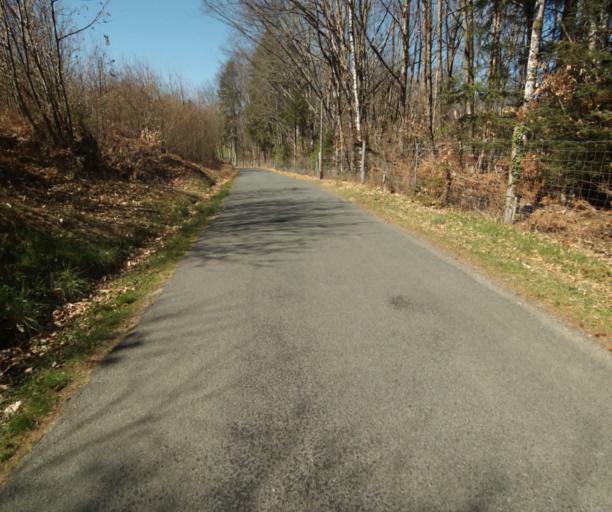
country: FR
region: Limousin
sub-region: Departement de la Correze
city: Chameyrat
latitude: 45.2703
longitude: 1.7070
